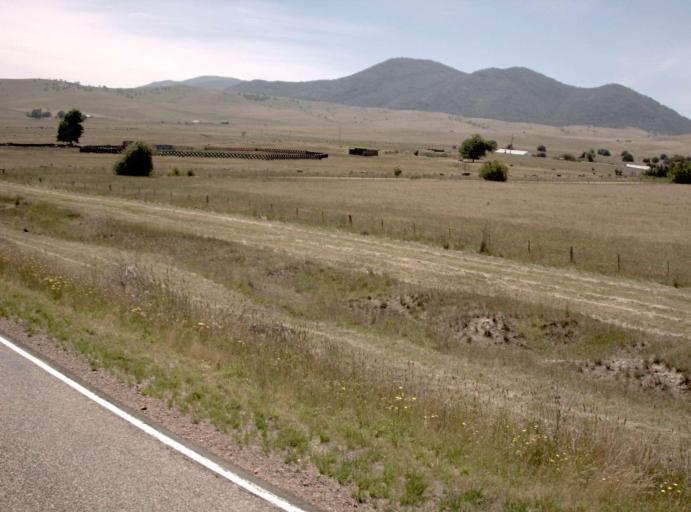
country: AU
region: Victoria
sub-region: Alpine
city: Mount Beauty
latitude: -37.0036
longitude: 147.6660
